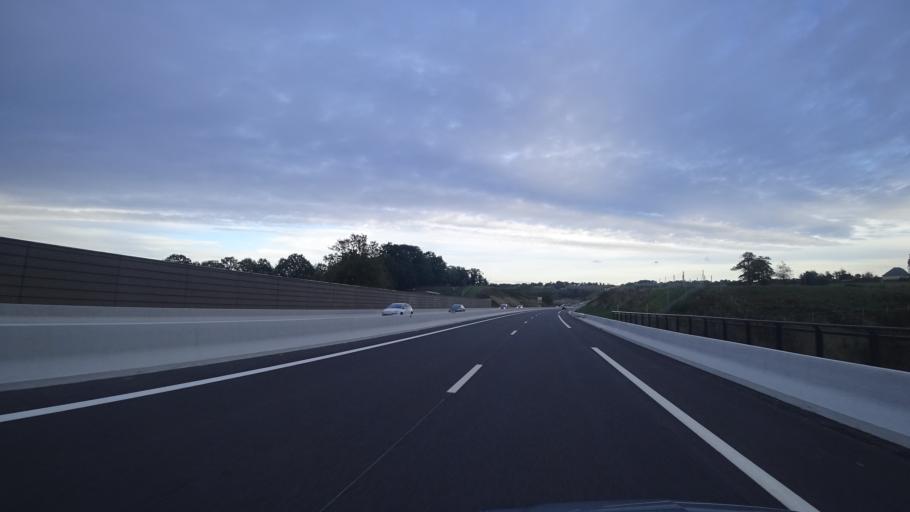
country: FR
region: Midi-Pyrenees
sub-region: Departement de l'Aveyron
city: Baraqueville
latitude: 44.2924
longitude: 2.4442
